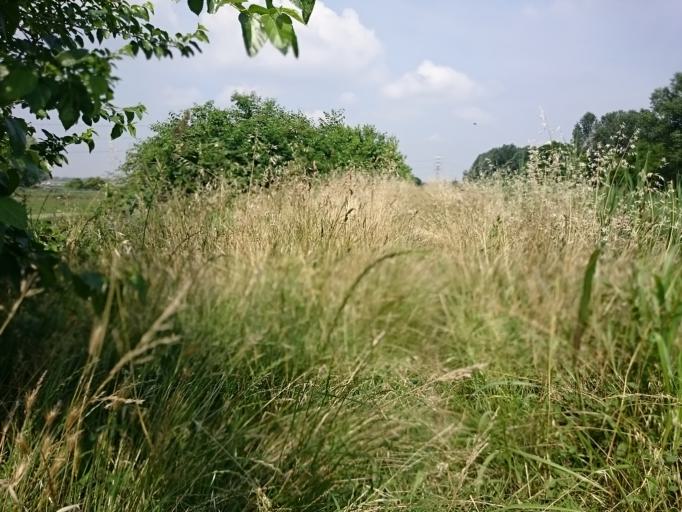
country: IT
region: Veneto
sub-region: Provincia di Padova
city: Codevigo
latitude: 45.2566
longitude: 12.1315
